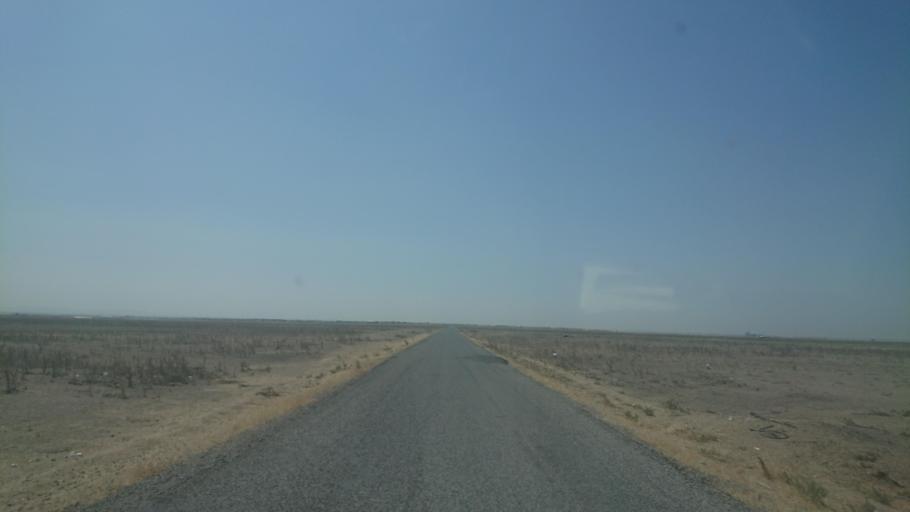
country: TR
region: Aksaray
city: Yesilova
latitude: 38.3208
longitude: 33.7434
